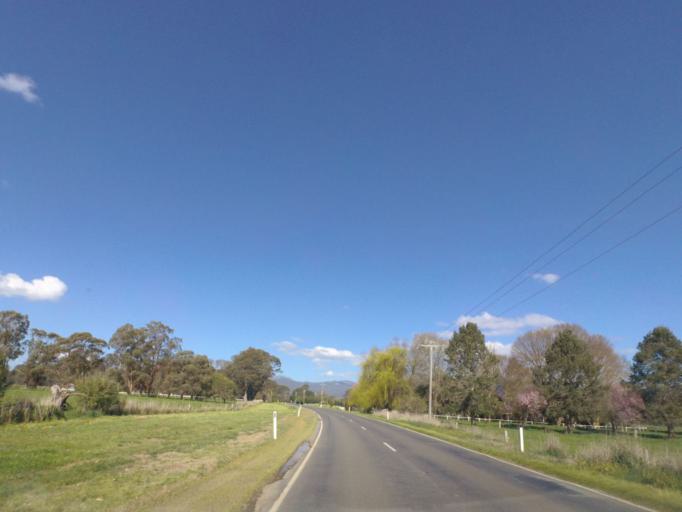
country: AU
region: Victoria
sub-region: Murrindindi
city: Alexandra
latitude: -37.2430
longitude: 145.7708
